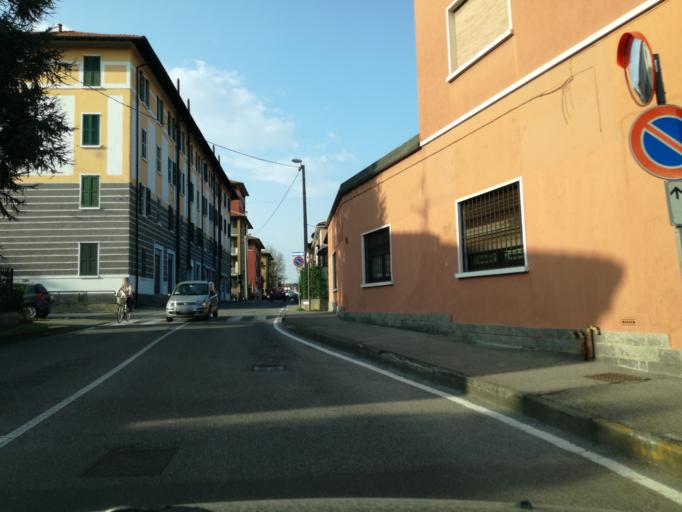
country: IT
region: Lombardy
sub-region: Provincia di Monza e Brianza
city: Carnate
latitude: 45.6474
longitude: 9.3785
